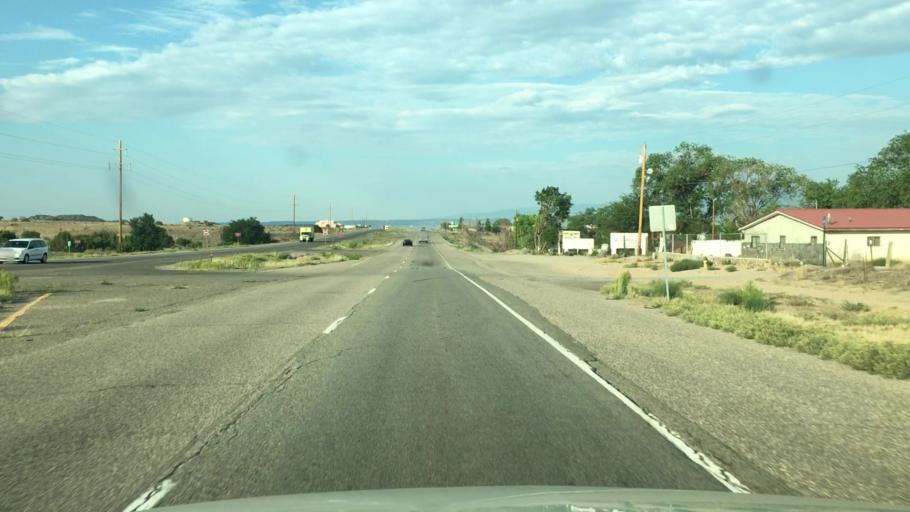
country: US
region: New Mexico
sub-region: Rio Arriba County
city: Ohkay Owingeh
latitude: 36.1124
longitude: -106.0248
